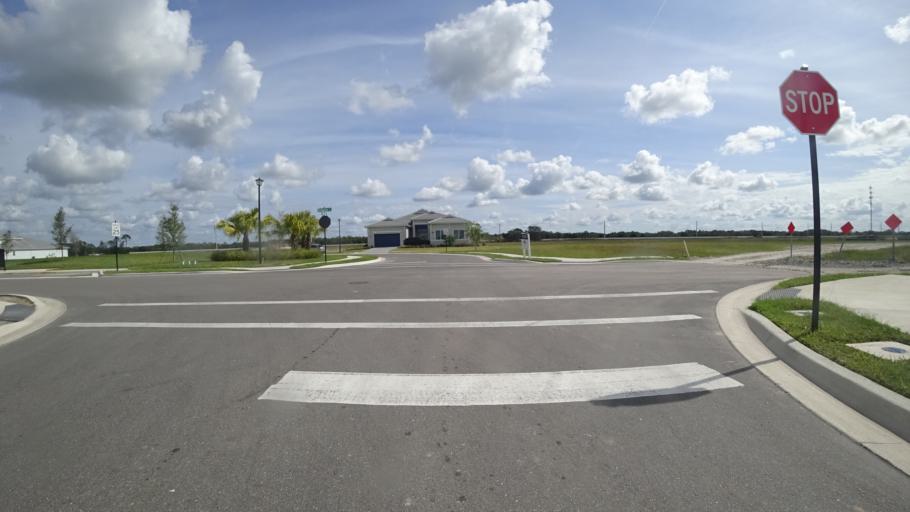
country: US
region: Florida
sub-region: Sarasota County
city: The Meadows
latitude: 27.3954
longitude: -82.3579
